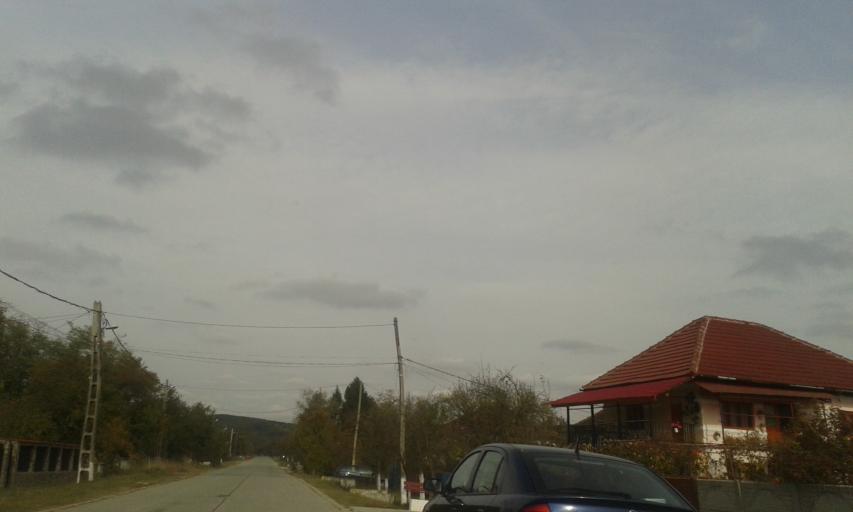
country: RO
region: Gorj
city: Logresti
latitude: 44.8756
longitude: 23.7082
